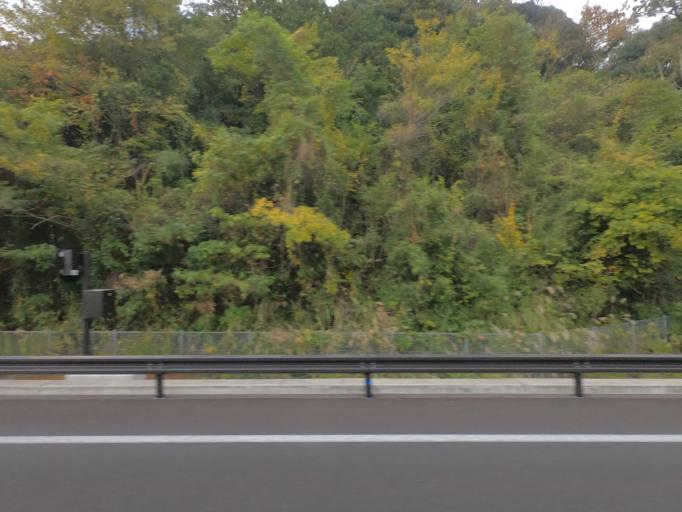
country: JP
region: Kumamoto
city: Minamata
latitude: 32.2350
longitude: 130.4556
